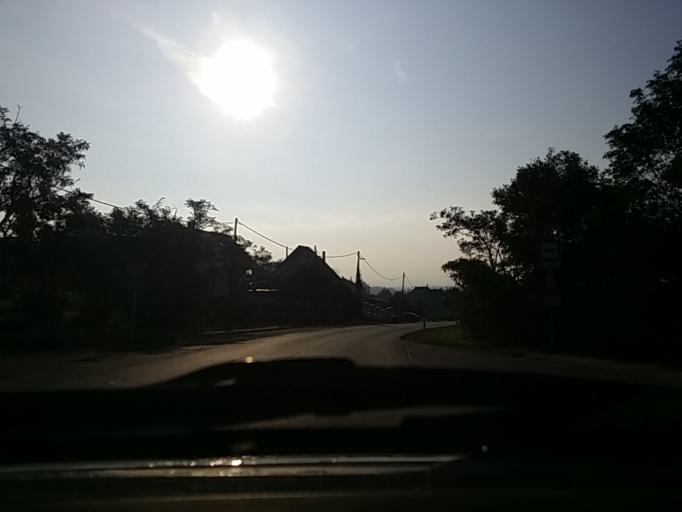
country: HU
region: Pest
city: Nagykovacsi
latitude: 47.7002
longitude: 19.0308
